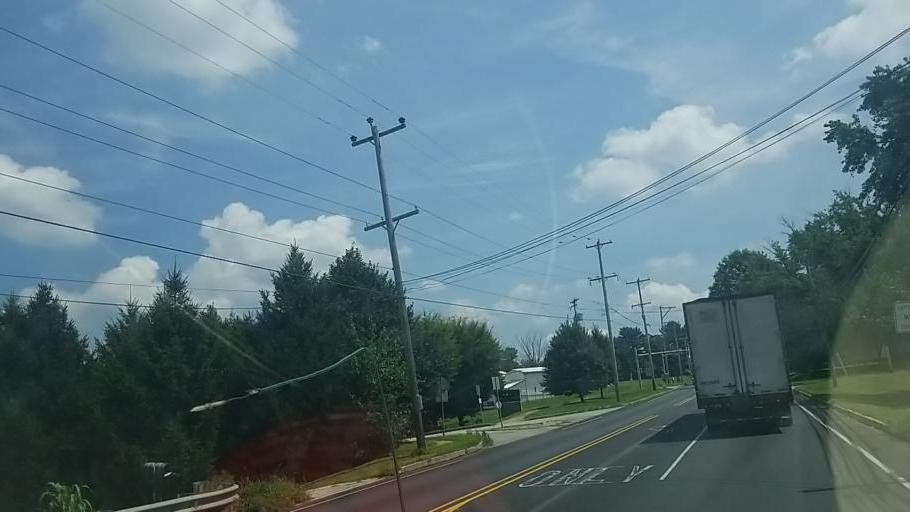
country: US
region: Pennsylvania
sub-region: Chester County
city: Avondale
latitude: 39.8169
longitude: -75.7693
